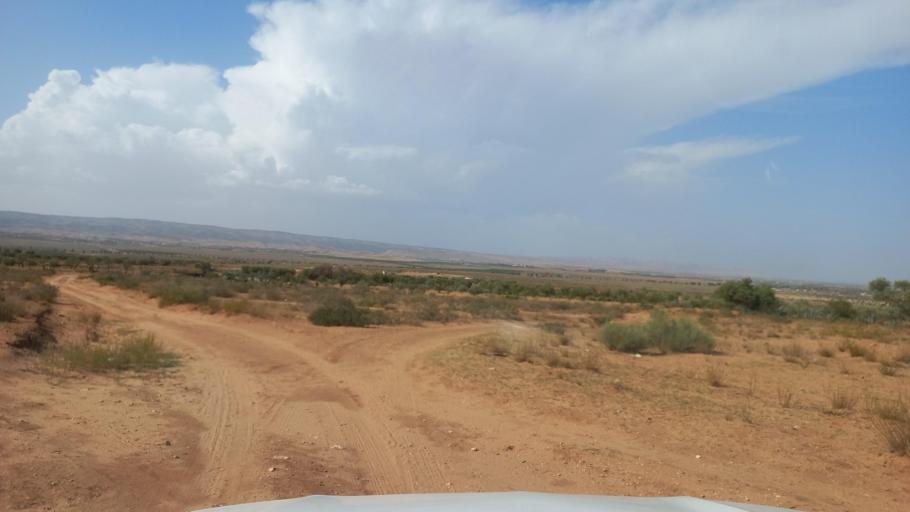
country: TN
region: Al Qasrayn
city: Kasserine
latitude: 35.2091
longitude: 8.9783
